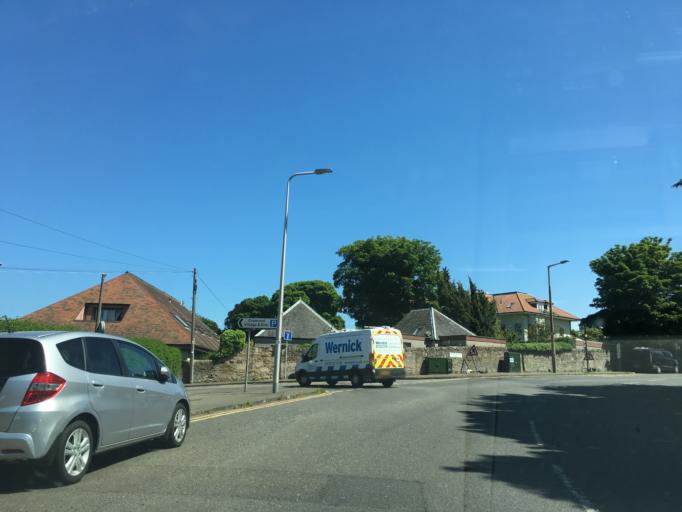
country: GB
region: Scotland
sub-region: Fife
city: Aberdour
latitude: 55.9754
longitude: -3.2999
